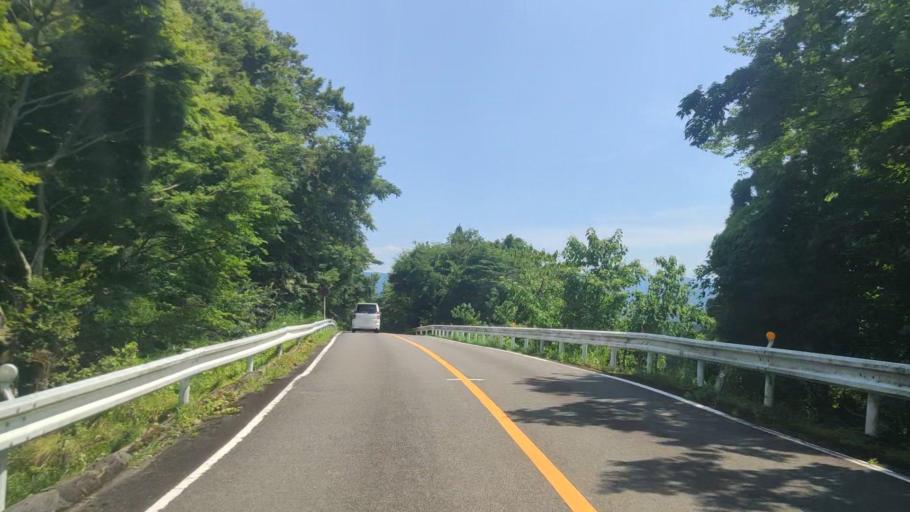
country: JP
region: Gifu
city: Tarui
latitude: 35.3772
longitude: 136.4451
